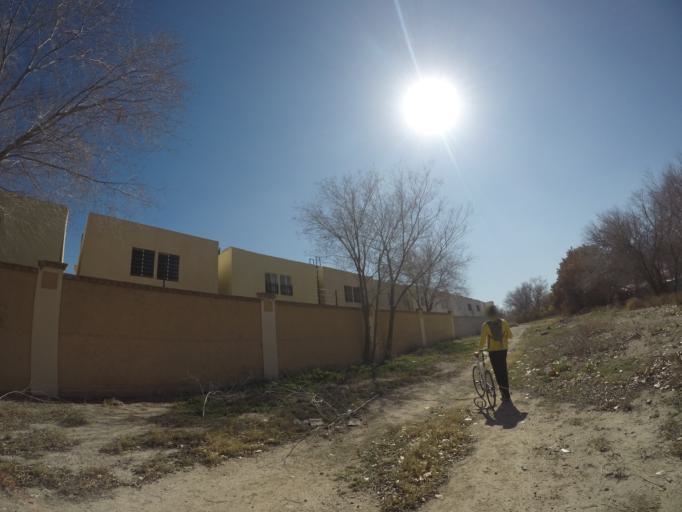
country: US
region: Texas
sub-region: El Paso County
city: Socorro
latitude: 31.6642
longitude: -106.3768
